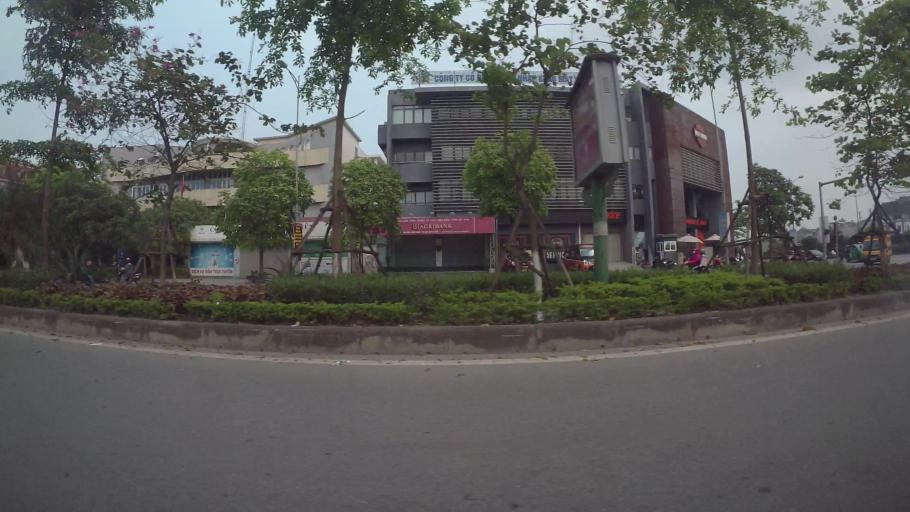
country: VN
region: Ha Noi
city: Hoan Kiem
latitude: 21.0578
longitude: 105.8905
